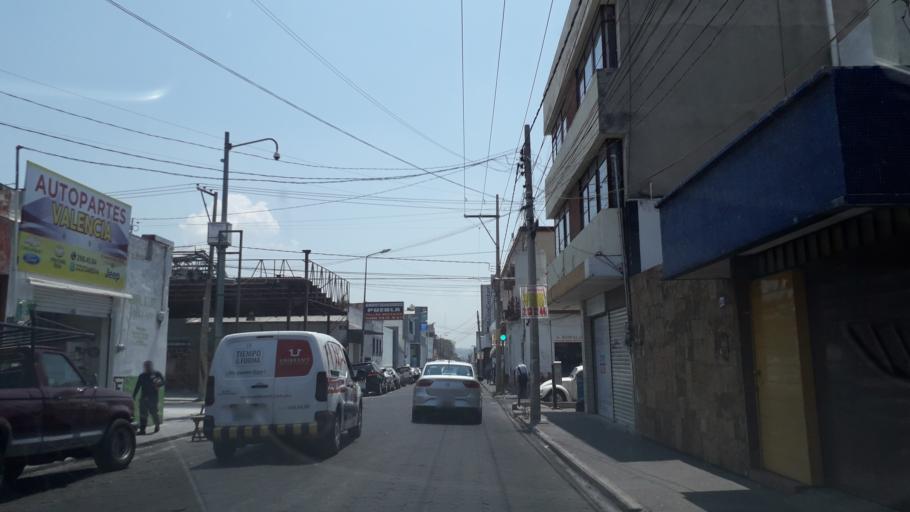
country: MX
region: Puebla
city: Puebla
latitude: 19.0529
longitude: -98.2154
